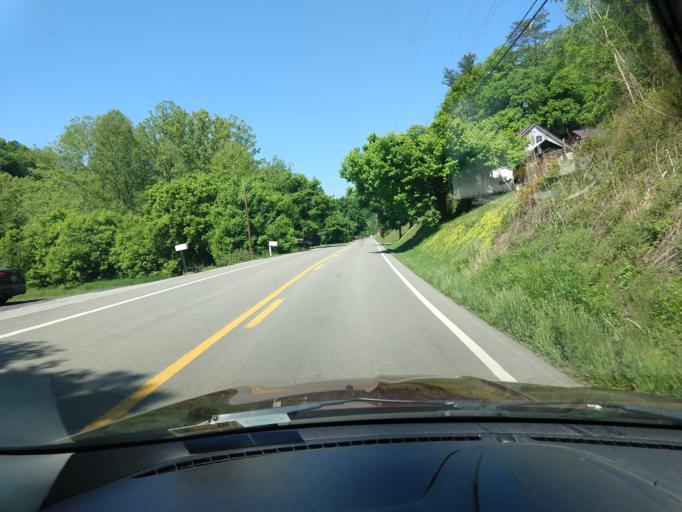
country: US
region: West Virginia
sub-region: Gilmer County
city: Glenville
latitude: 38.9155
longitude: -80.7585
